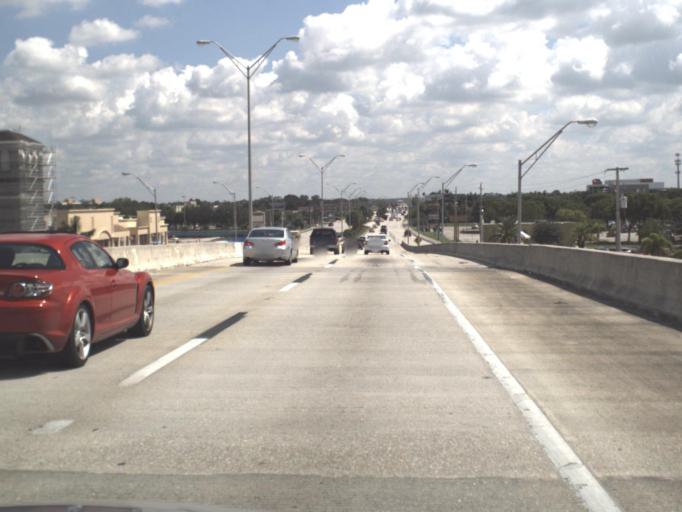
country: US
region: Florida
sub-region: Lee County
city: Pine Manor
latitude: 26.5968
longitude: -81.8713
